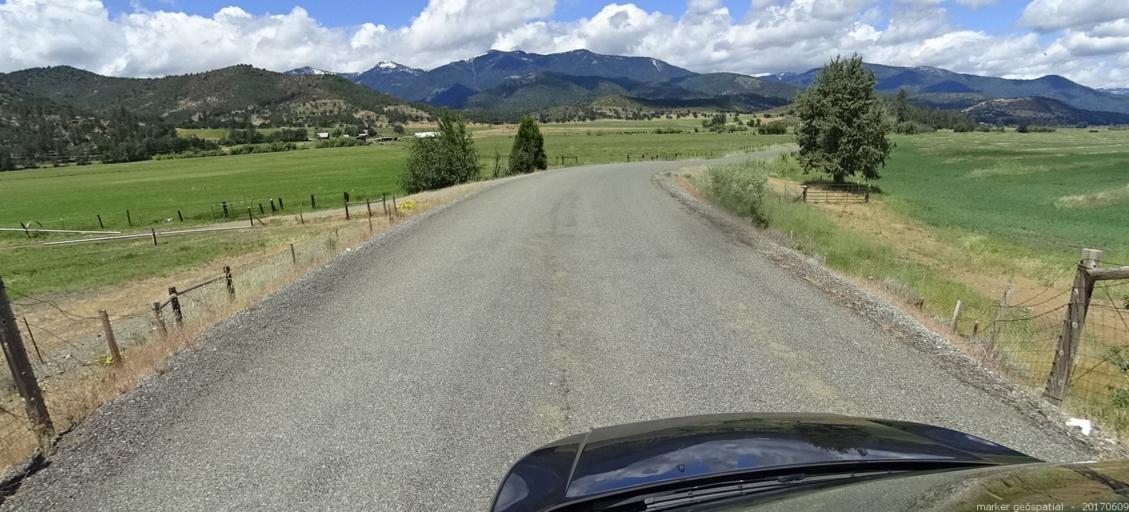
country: US
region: California
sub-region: Siskiyou County
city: Yreka
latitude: 41.3960
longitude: -122.8337
